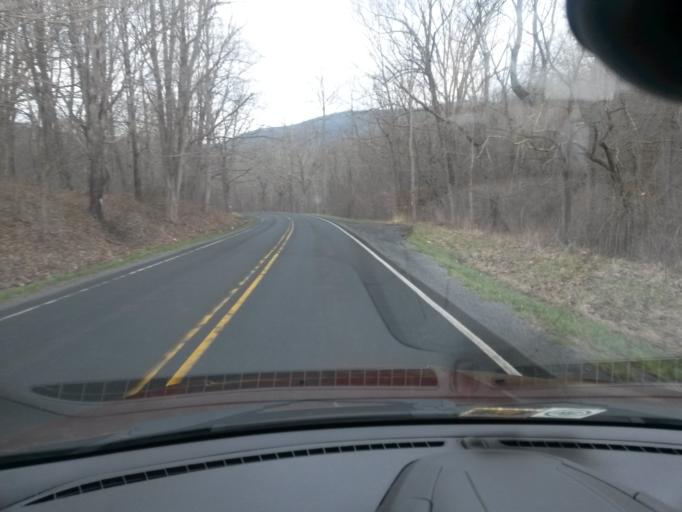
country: US
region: Virginia
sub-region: Bath County
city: Warm Springs
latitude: 38.0669
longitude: -79.7734
